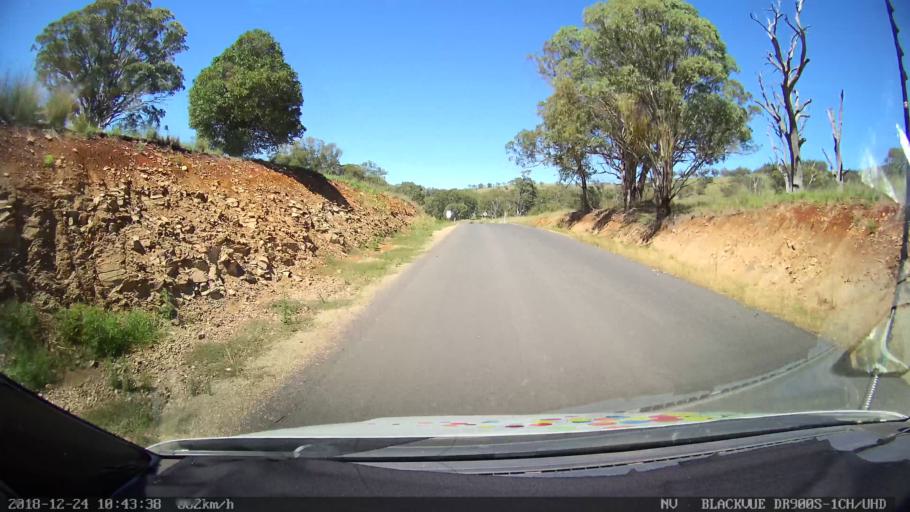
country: AU
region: New South Wales
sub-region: Upper Hunter Shire
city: Merriwa
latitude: -31.8842
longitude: 150.4451
